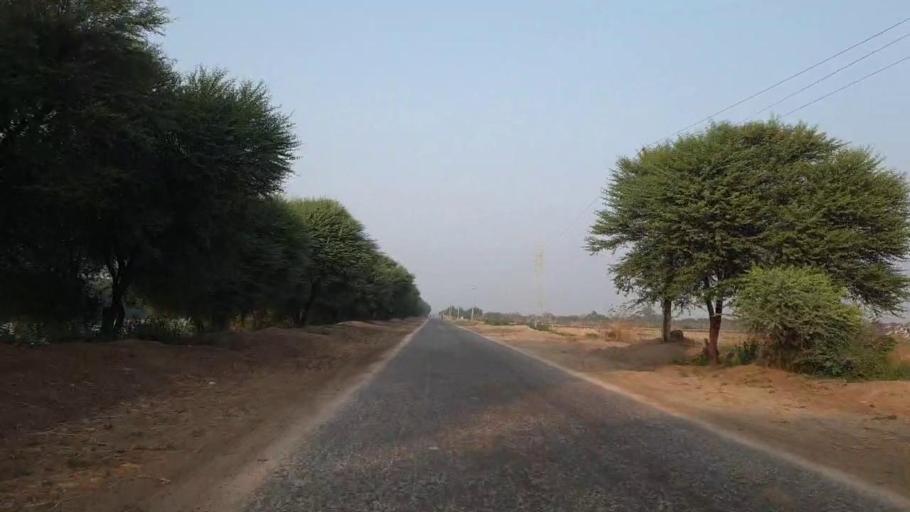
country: PK
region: Sindh
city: Tando Muhammad Khan
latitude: 25.1233
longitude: 68.4301
